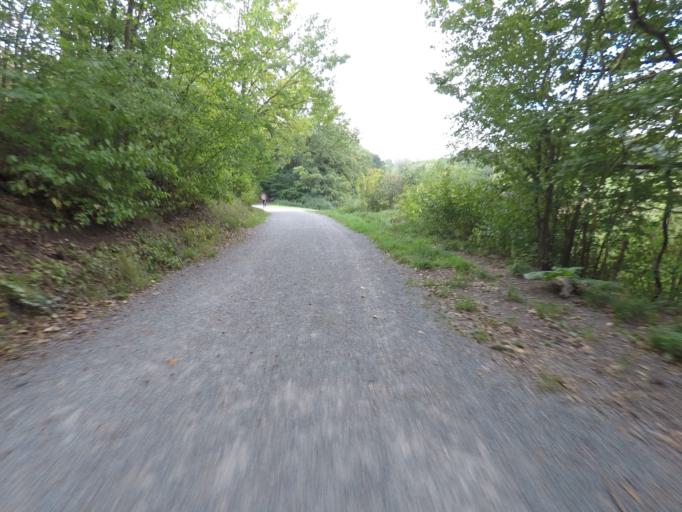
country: DE
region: Baden-Wuerttemberg
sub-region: Regierungsbezirk Stuttgart
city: Boeblingen
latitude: 48.6714
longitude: 8.9895
